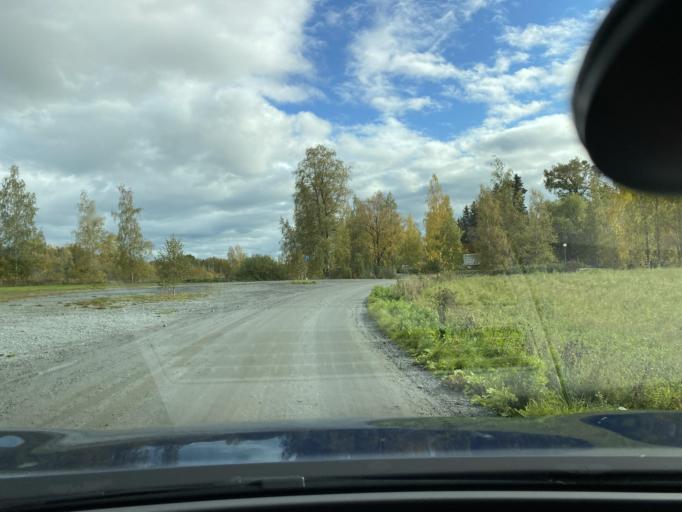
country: FI
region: Pirkanmaa
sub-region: Tampere
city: Nokia
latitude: 61.4715
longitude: 23.3547
